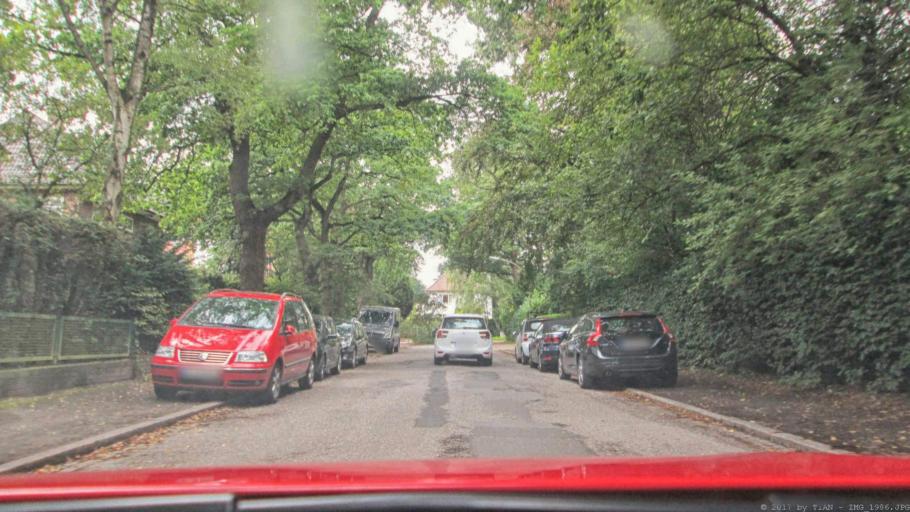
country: DE
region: Hamburg
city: Altona
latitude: 53.5574
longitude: 9.8832
